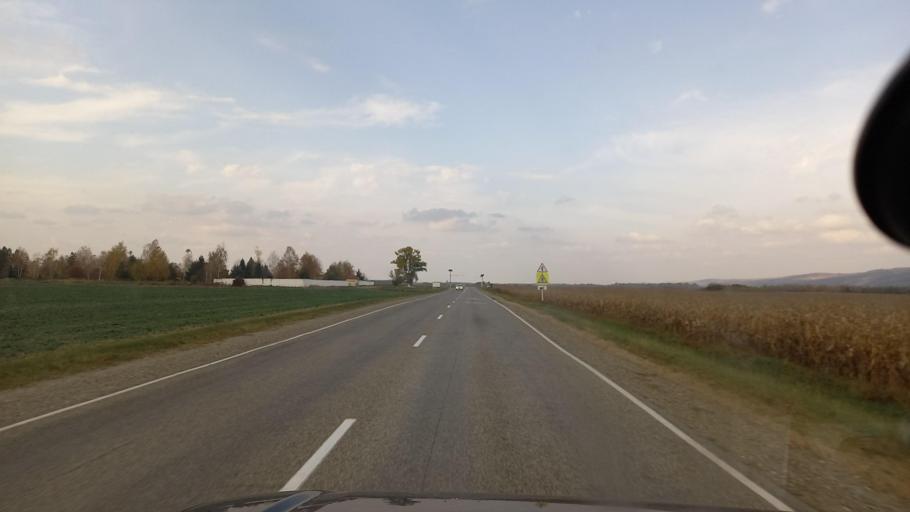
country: RU
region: Krasnodarskiy
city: Perepravnaya
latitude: 44.3463
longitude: 40.8415
